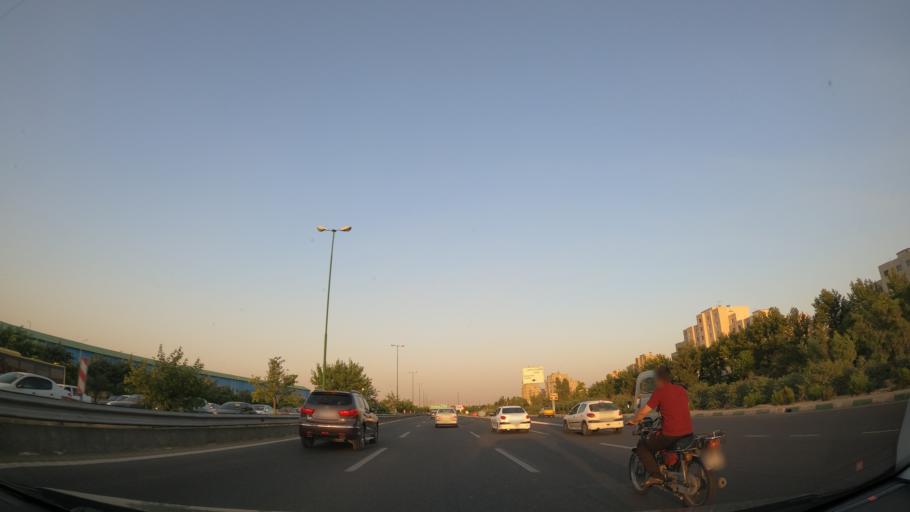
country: IR
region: Tehran
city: Tehran
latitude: 35.7147
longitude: 51.3236
